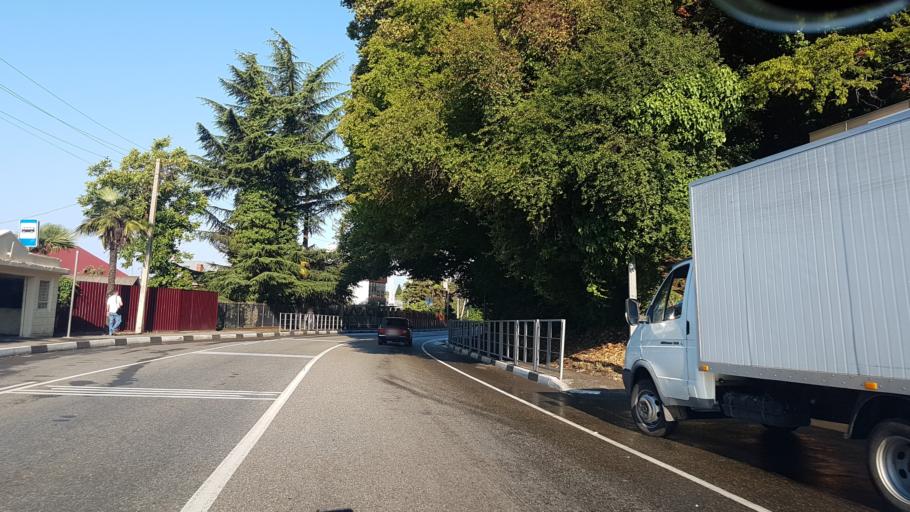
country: RU
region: Krasnodarskiy
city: Vardane
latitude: 43.7987
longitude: 39.4652
